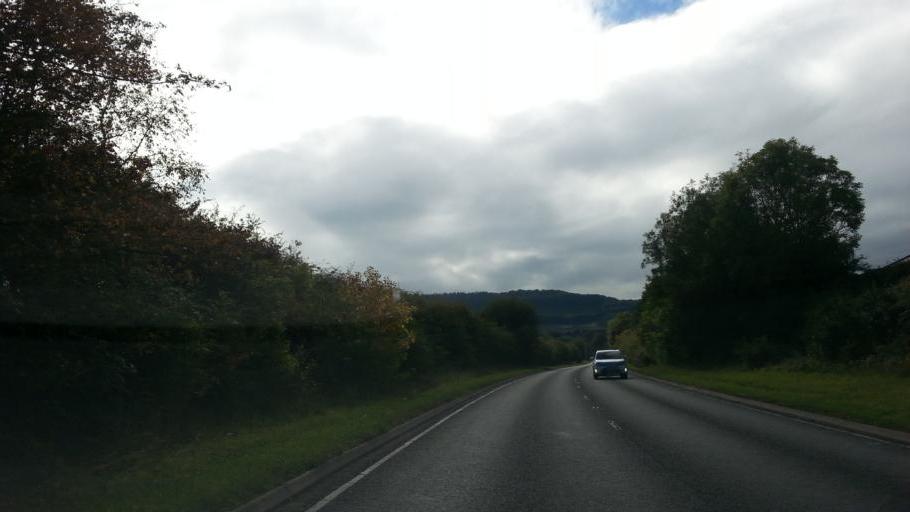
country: GB
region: England
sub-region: Herefordshire
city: Ross on Wye
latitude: 51.9250
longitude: -2.5710
